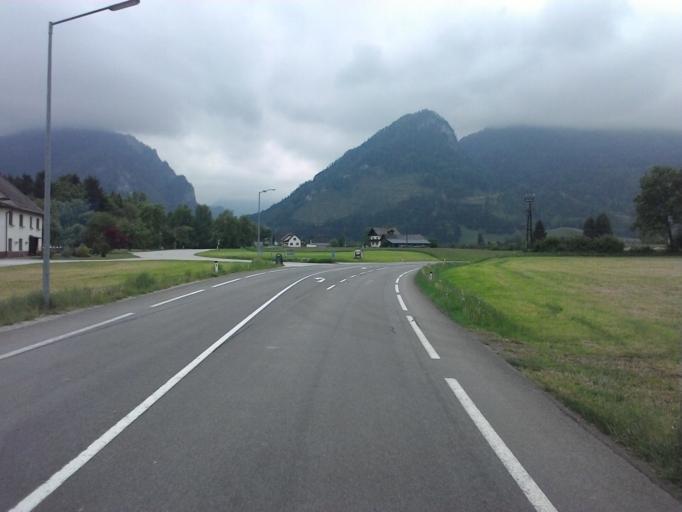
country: AT
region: Styria
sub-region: Politischer Bezirk Liezen
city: Gams bei Hieflau
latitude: 47.6496
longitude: 14.7631
